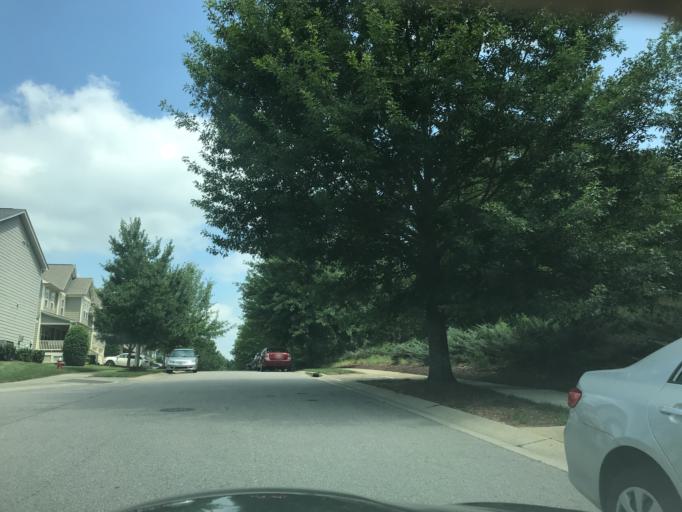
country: US
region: North Carolina
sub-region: Wake County
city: Wake Forest
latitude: 35.9212
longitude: -78.5603
